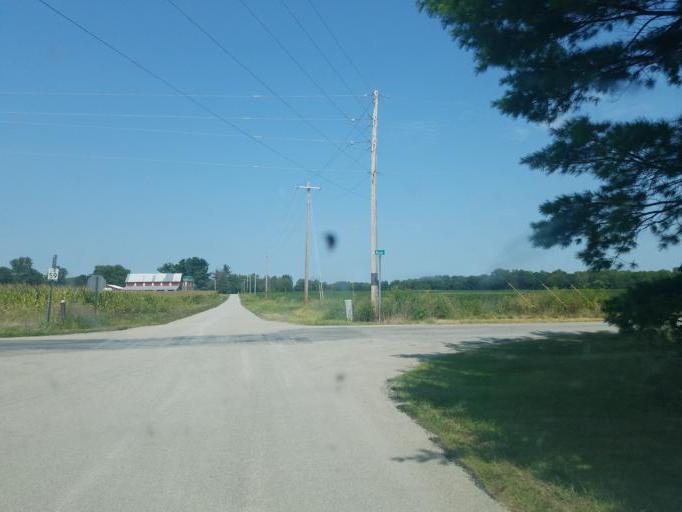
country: US
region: Ohio
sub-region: Crawford County
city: Bucyrus
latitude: 40.7896
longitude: -83.1120
